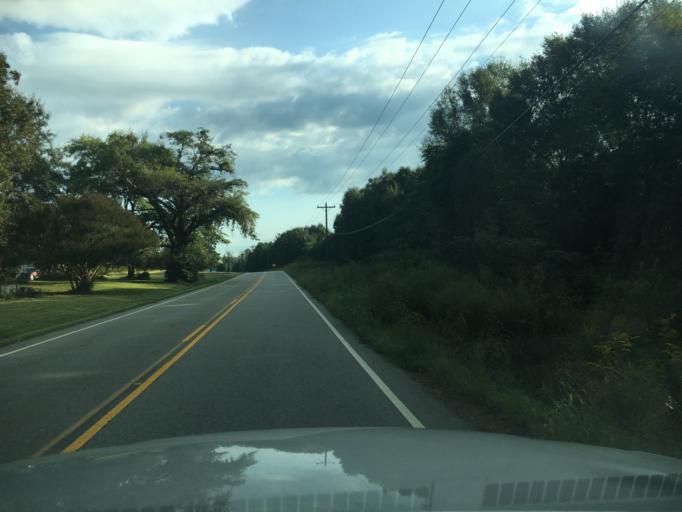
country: US
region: South Carolina
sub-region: Spartanburg County
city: Wellford
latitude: 34.9206
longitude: -82.1060
